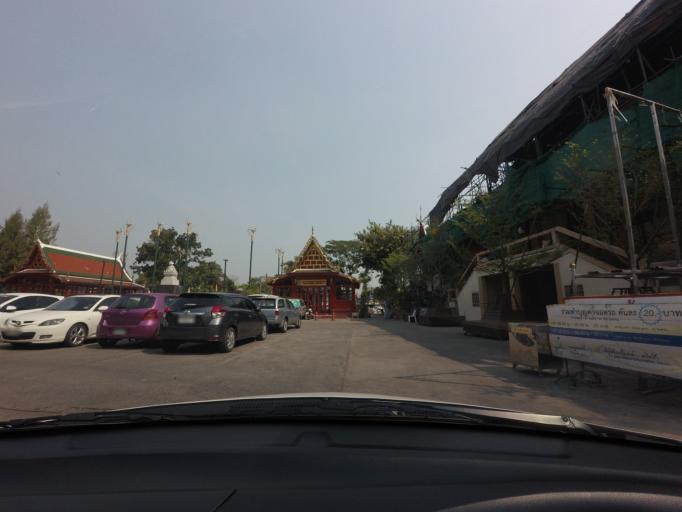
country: TH
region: Bangkok
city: Bangkok Noi
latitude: 13.7635
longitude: 100.4772
